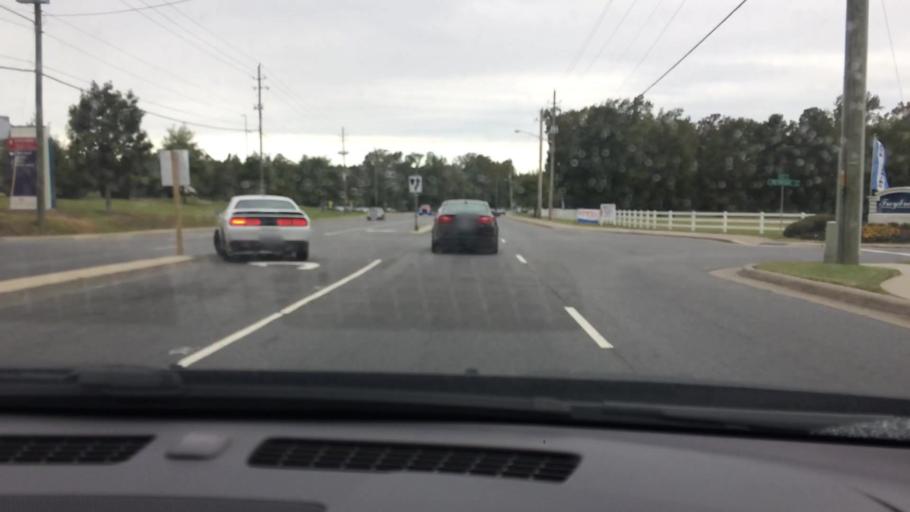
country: US
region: North Carolina
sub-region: Pitt County
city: Greenville
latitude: 35.6139
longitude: -77.4038
